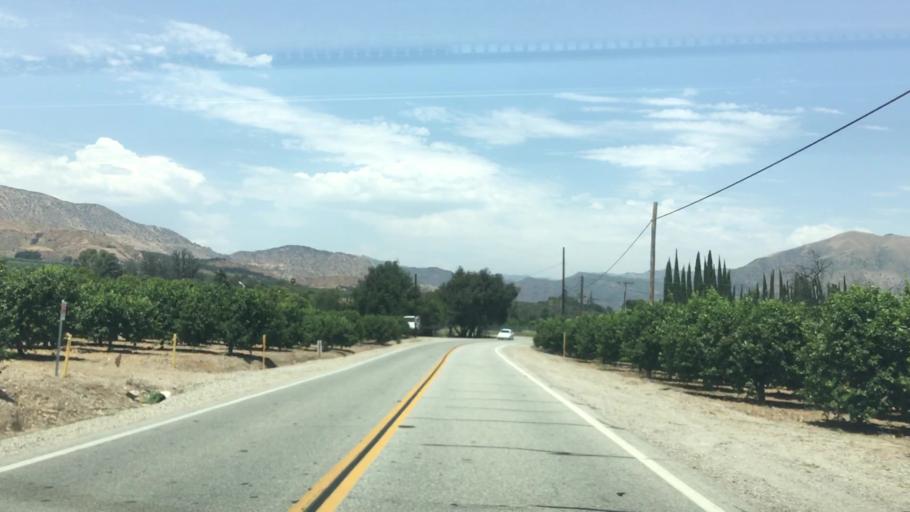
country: US
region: California
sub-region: Ventura County
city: Fillmore
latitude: 34.4023
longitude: -118.9473
